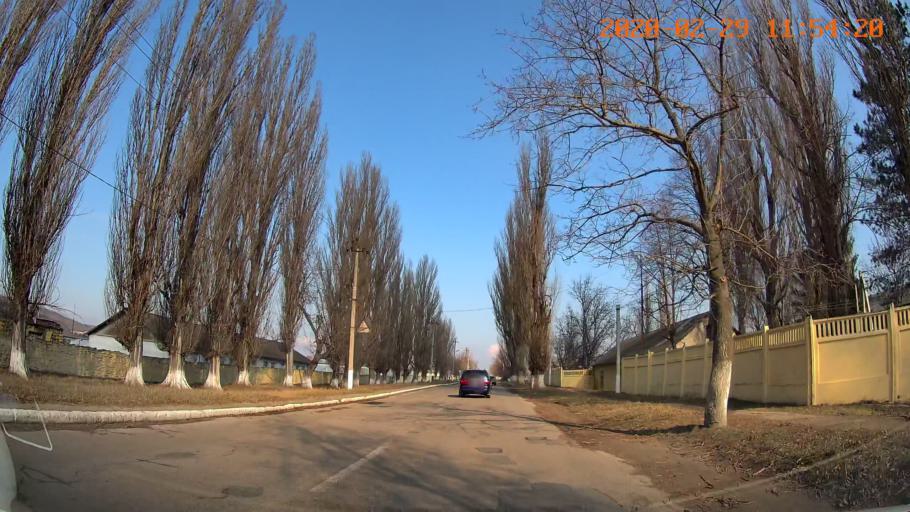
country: MD
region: Telenesti
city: Ribnita
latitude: 47.7837
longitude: 28.9947
